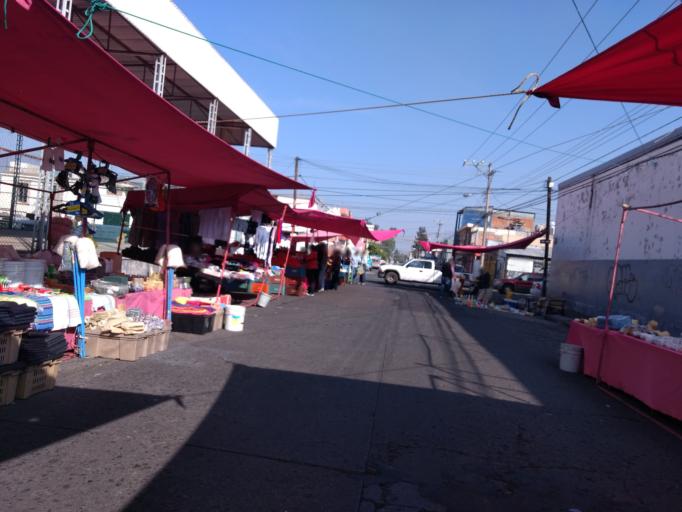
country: MX
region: Michoacan
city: Morelia
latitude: 19.7028
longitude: -101.2107
